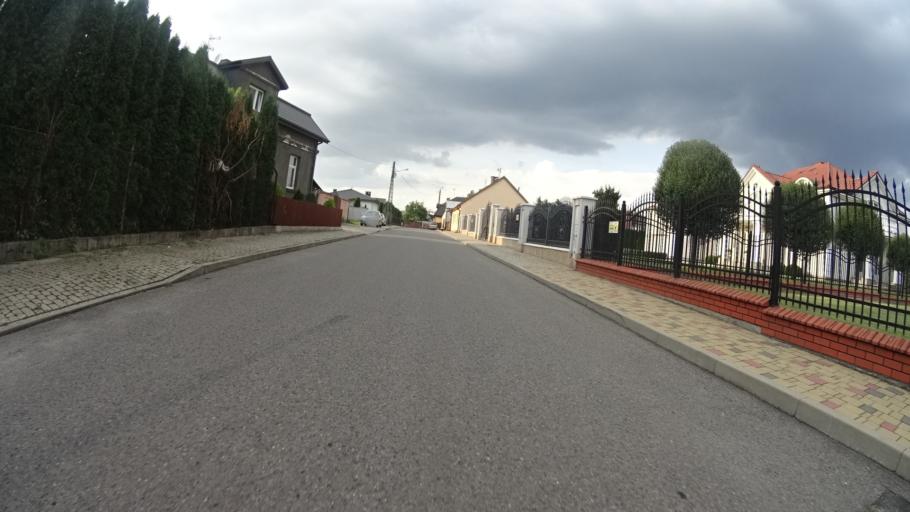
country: PL
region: Masovian Voivodeship
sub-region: Powiat grojecki
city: Mogielnica
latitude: 51.6917
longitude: 20.7241
